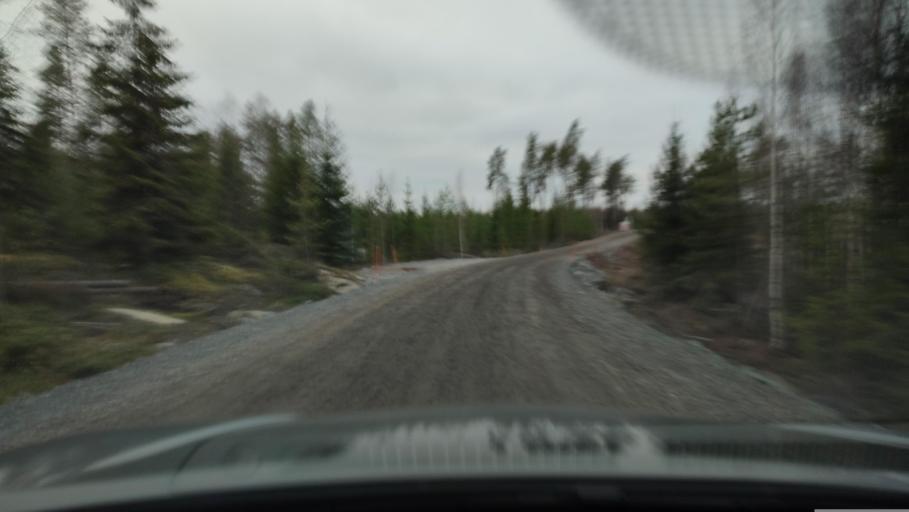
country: FI
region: Ostrobothnia
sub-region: Sydosterbotten
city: Kristinestad
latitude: 62.1910
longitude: 21.5234
